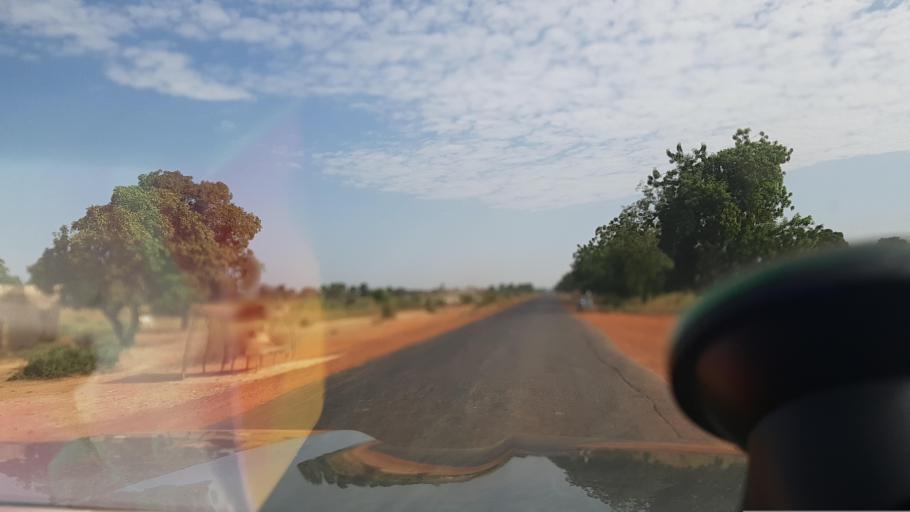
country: ML
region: Segou
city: Segou
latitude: 13.5053
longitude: -6.1471
